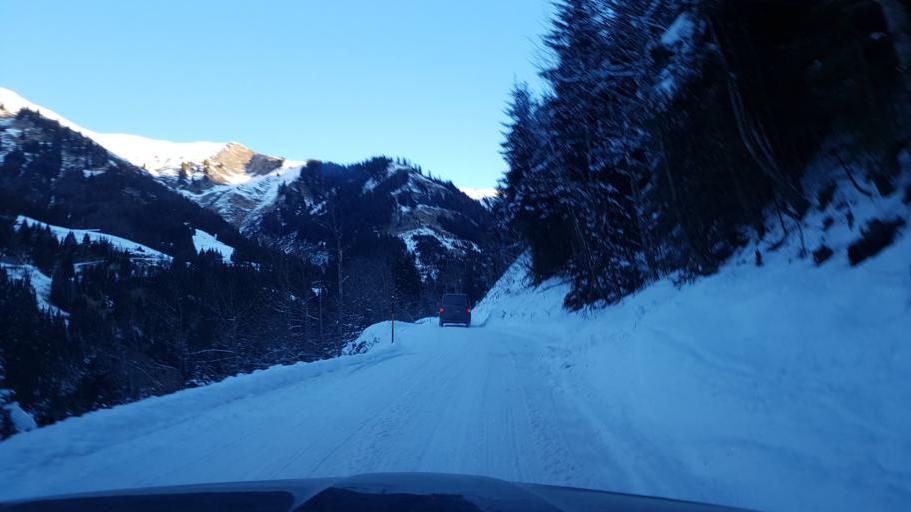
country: AT
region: Salzburg
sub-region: Politischer Bezirk Sankt Johann im Pongau
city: Huttschlag
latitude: 47.1761
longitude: 13.2667
